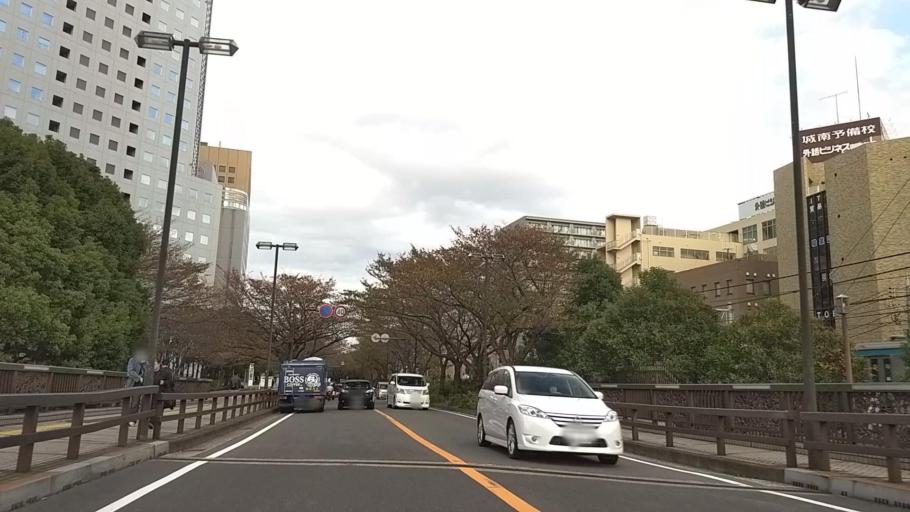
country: JP
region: Kanagawa
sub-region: Kawasaki-shi
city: Kawasaki
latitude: 35.5340
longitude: 139.6998
